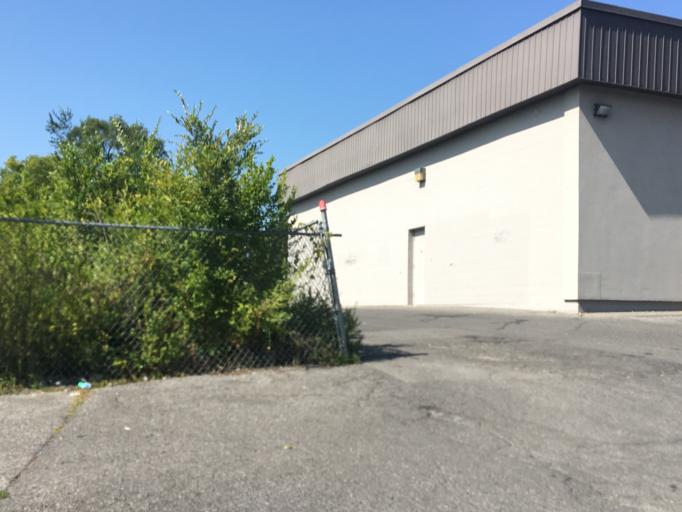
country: CA
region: Ontario
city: Ottawa
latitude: 45.3772
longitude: -75.6446
